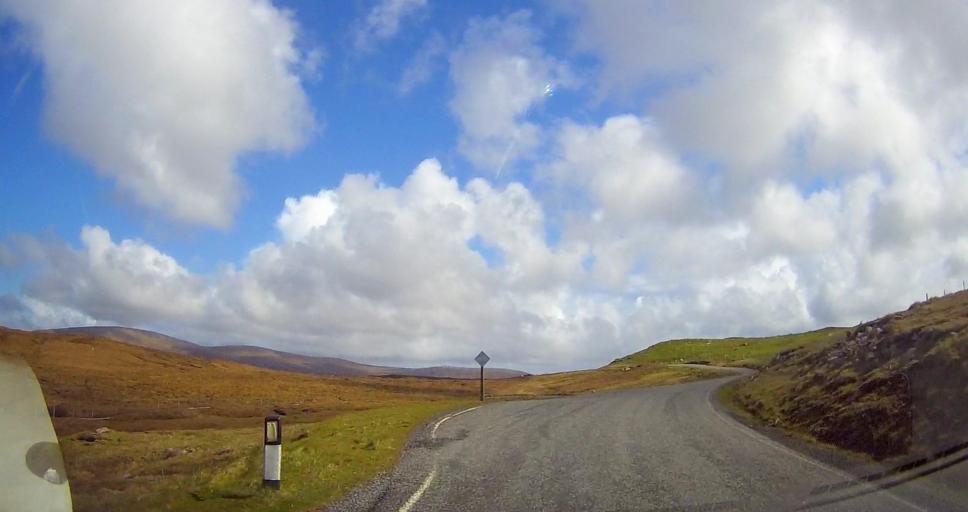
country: GB
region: Scotland
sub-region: Shetland Islands
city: Lerwick
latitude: 60.4821
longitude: -1.4053
